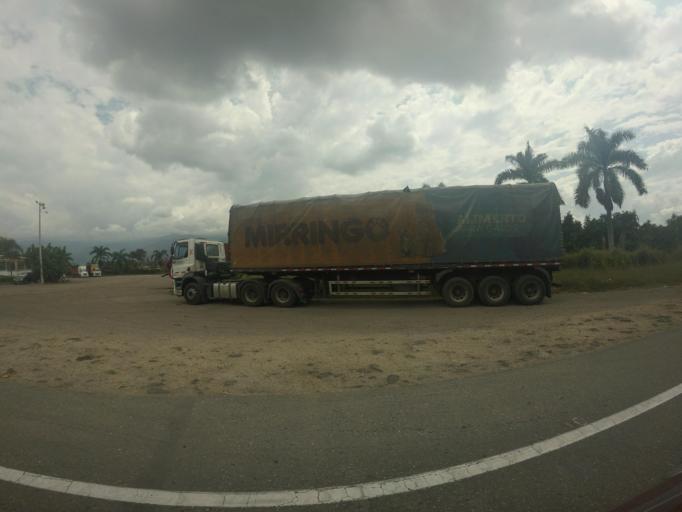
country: CO
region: Cundinamarca
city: Arbelaez
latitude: 4.3009
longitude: -74.4501
